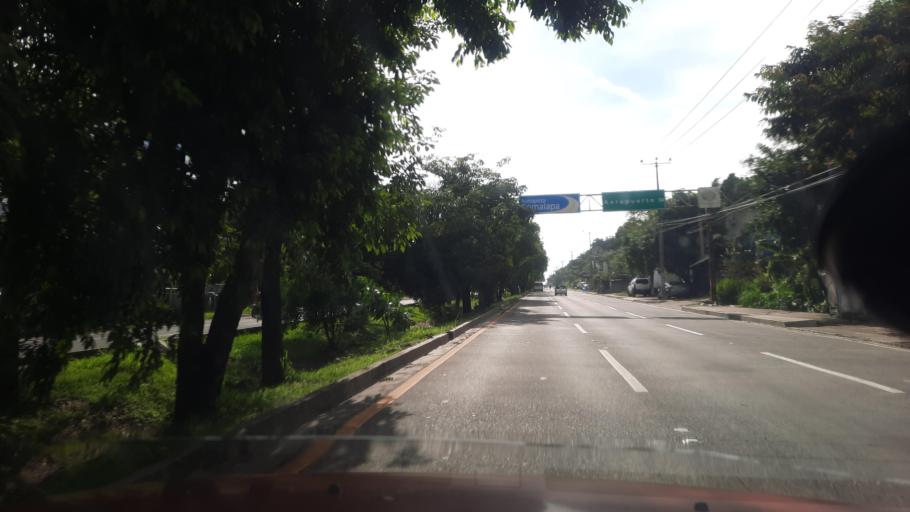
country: SV
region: San Salvador
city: San Marcos
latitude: 13.6497
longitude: -89.1790
